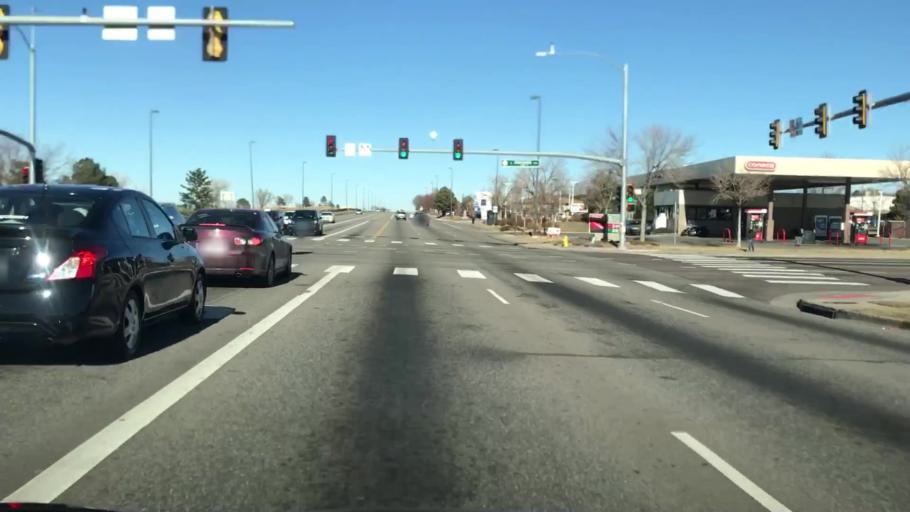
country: US
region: Colorado
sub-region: Adams County
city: Aurora
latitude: 39.7108
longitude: -104.8659
